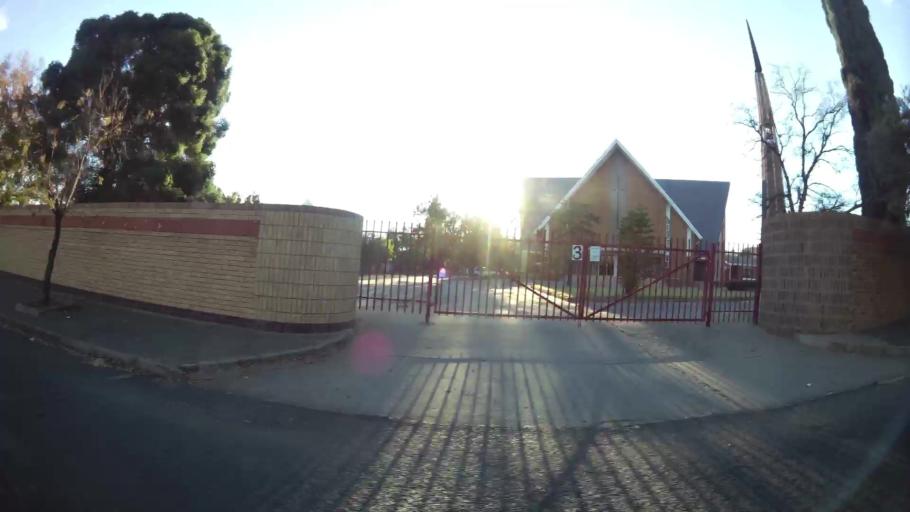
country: ZA
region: Northern Cape
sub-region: Frances Baard District Municipality
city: Kimberley
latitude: -28.7511
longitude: 24.7441
